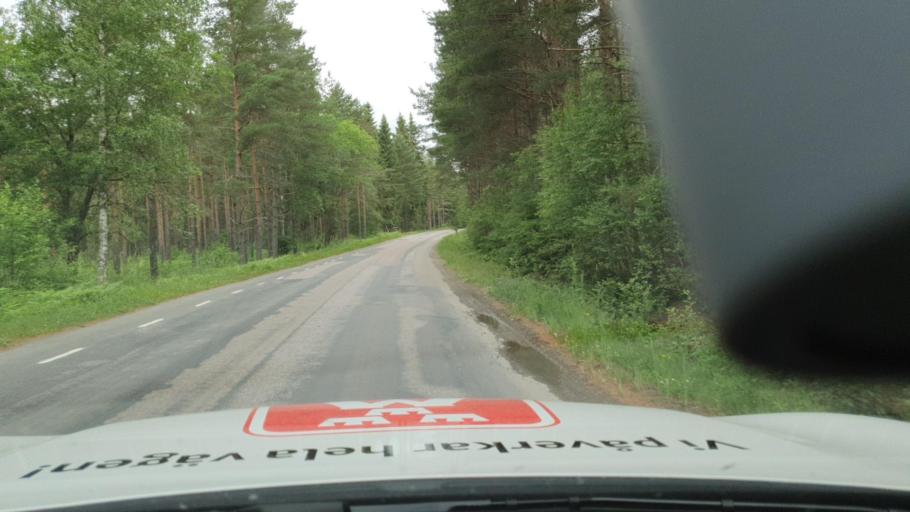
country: SE
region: Vaestra Goetaland
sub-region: Tidaholms Kommun
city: Olofstorp
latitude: 58.3213
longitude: 13.9987
